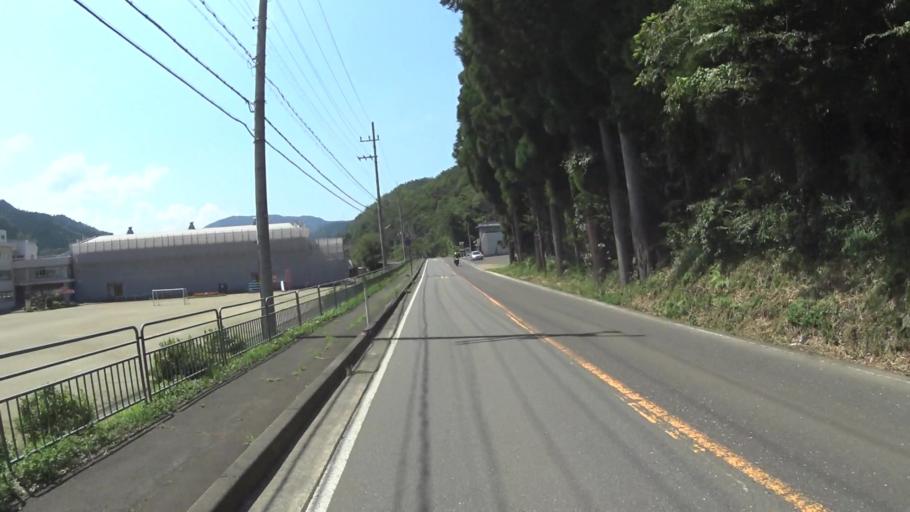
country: JP
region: Fukui
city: Obama
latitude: 35.4031
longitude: 135.6687
